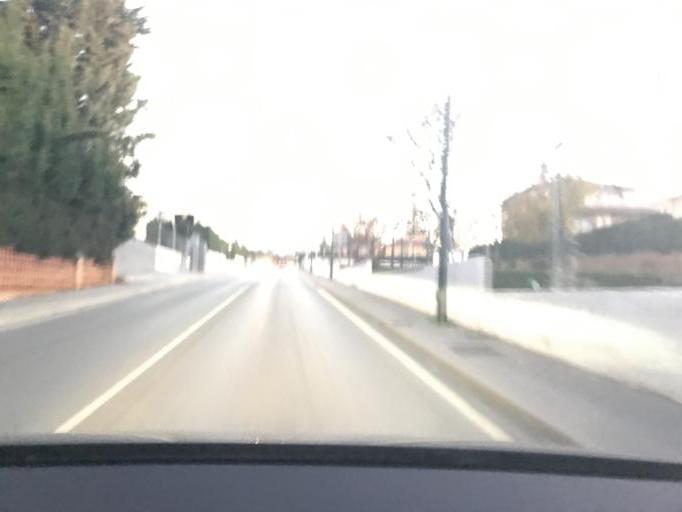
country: ES
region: Andalusia
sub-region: Provincia de Granada
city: Ogijares
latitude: 37.1156
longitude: -3.6031
